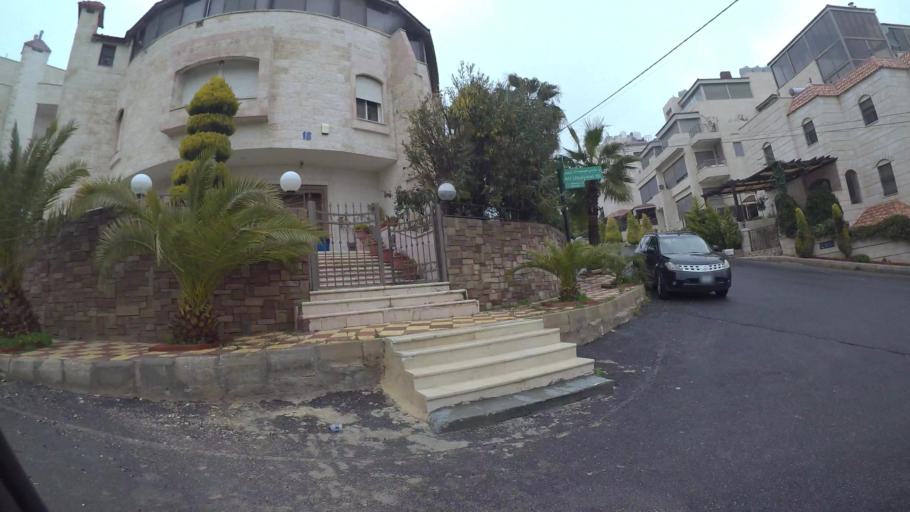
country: JO
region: Amman
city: Al Jubayhah
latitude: 32.0111
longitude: 35.8300
